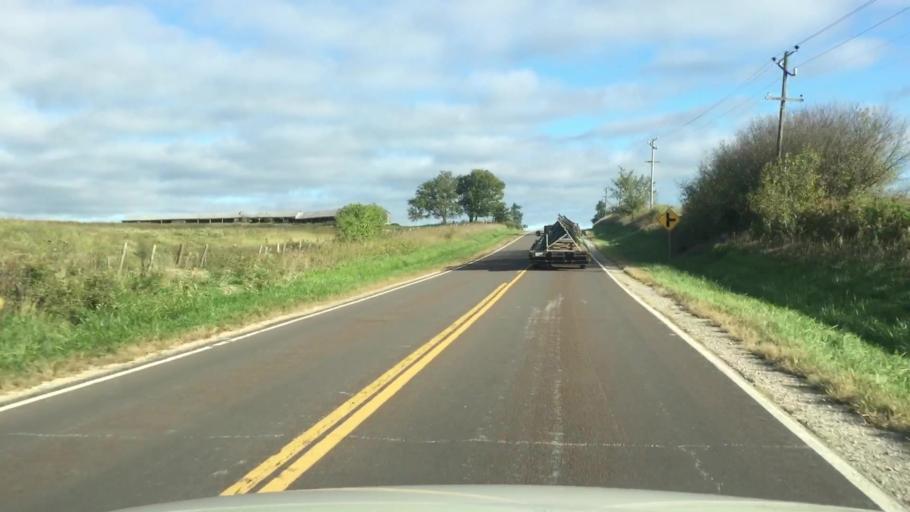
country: US
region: Missouri
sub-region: Howard County
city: New Franklin
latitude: 39.0735
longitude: -92.7458
